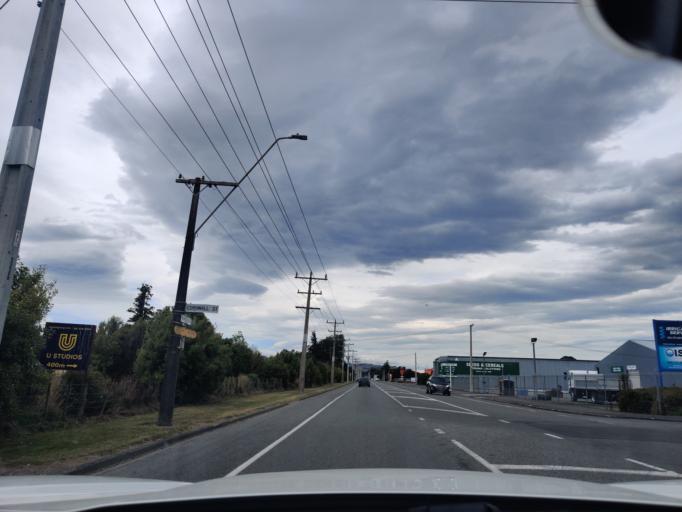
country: NZ
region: Wellington
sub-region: Masterton District
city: Masterton
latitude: -40.9492
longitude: 175.6329
